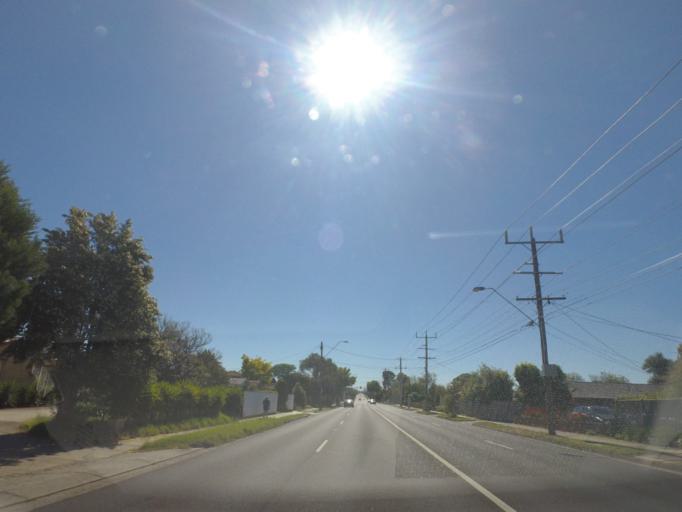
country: AU
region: Victoria
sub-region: Banyule
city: Bundoora
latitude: -37.7009
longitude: 145.0676
